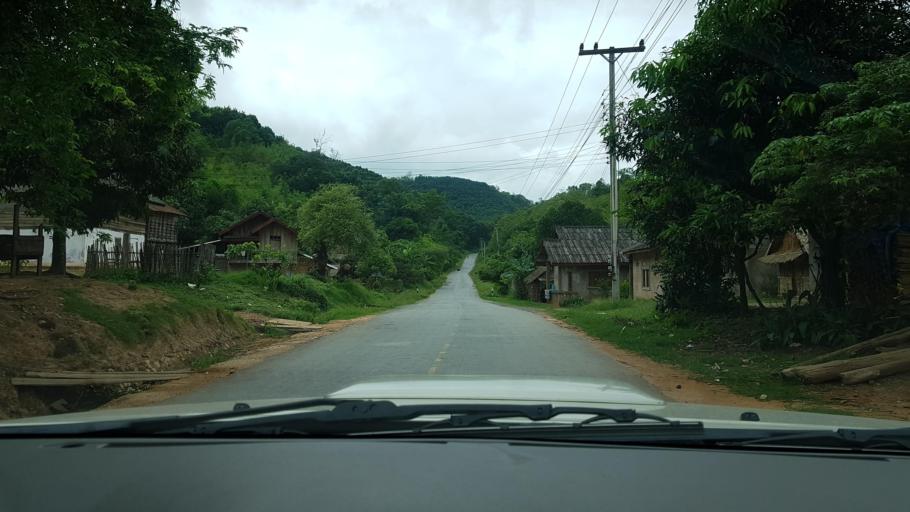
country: LA
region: Loungnamtha
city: Muang Nale
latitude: 20.3657
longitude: 101.7122
